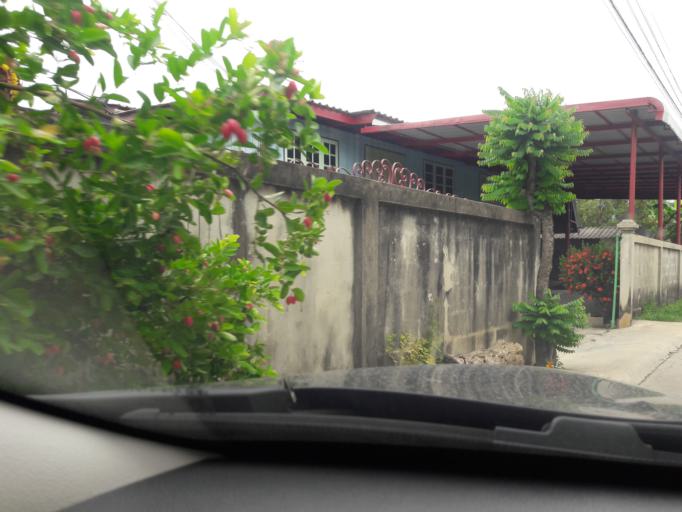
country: TH
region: Ratchaburi
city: Damnoen Saduak
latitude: 13.5981
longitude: 99.9085
